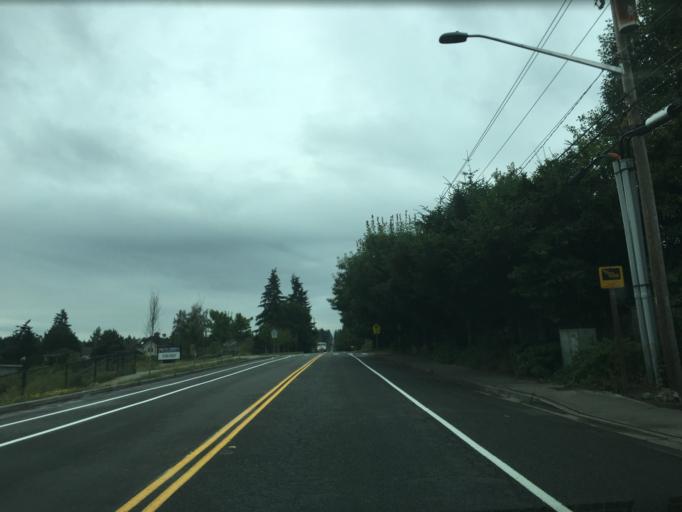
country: US
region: Washington
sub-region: King County
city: Inglewood-Finn Hill
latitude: 47.7159
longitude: -122.2295
